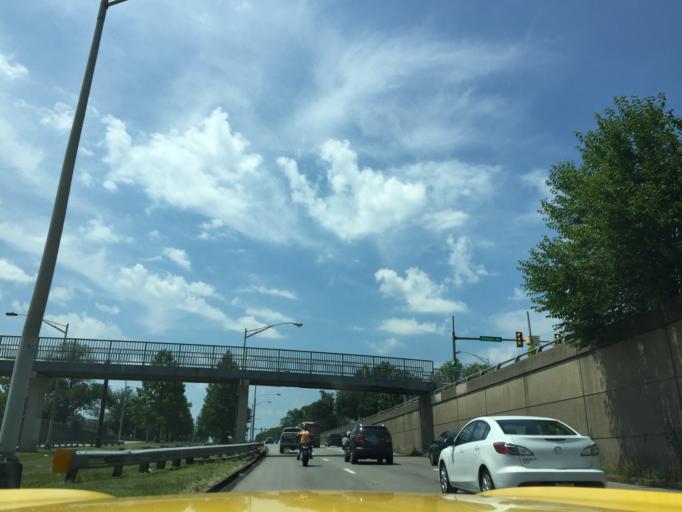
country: US
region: Pennsylvania
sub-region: Montgomery County
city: Rockledge
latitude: 40.0313
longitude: -75.0857
